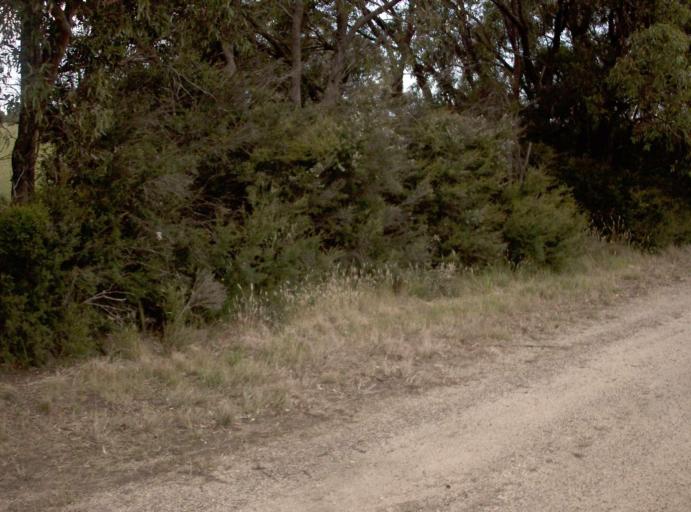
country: AU
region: Victoria
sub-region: Wellington
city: Sale
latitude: -38.1890
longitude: 147.0929
